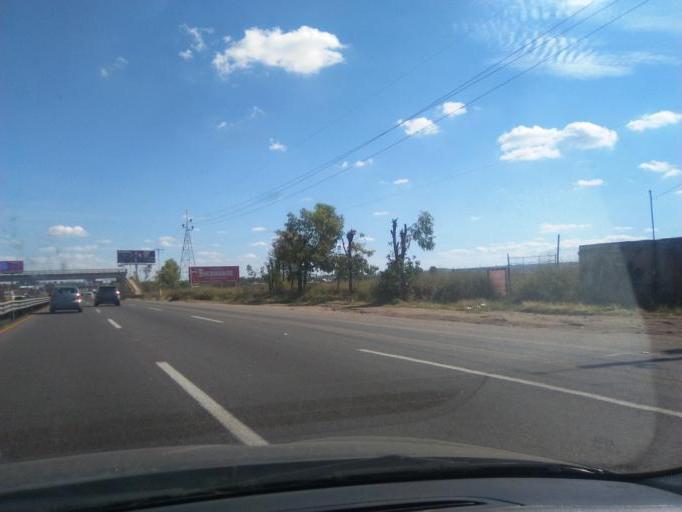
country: MX
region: Guanajuato
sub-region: Silao de la Victoria
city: El Refugio de los Sauces
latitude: 21.0114
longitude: -101.5227
